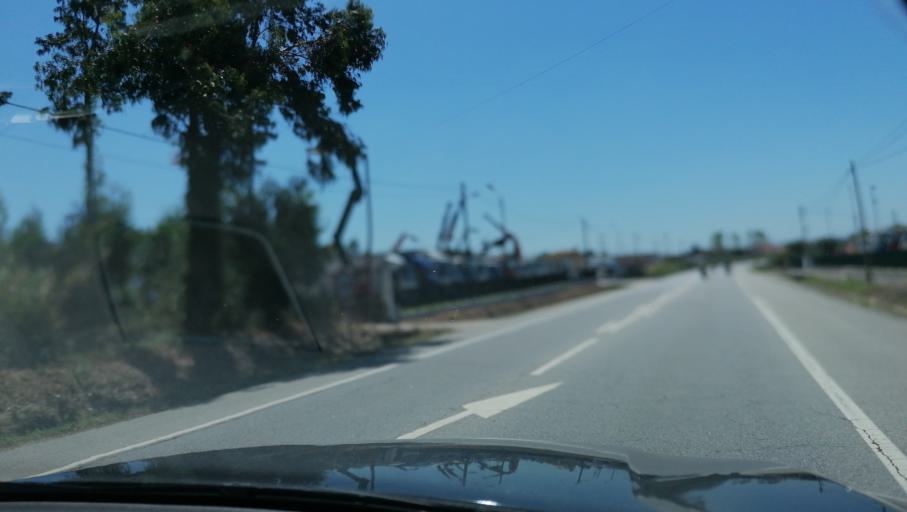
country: PT
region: Aveiro
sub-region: Anadia
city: Sangalhos
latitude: 40.4893
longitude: -8.4462
